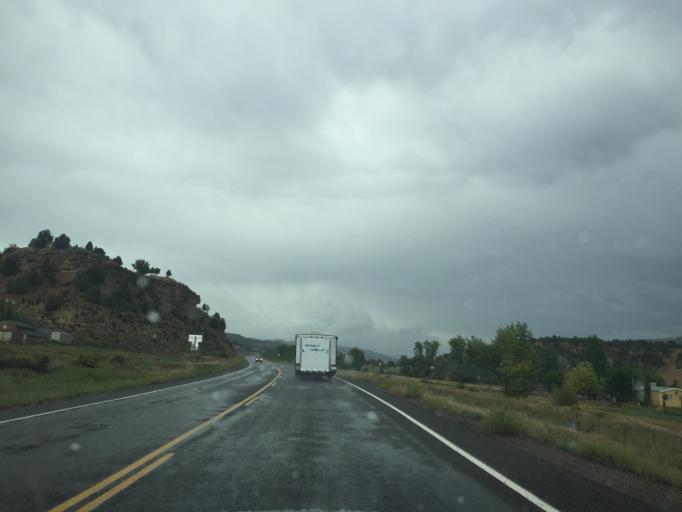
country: US
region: Utah
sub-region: Kane County
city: Kanab
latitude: 37.2267
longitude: -112.6781
